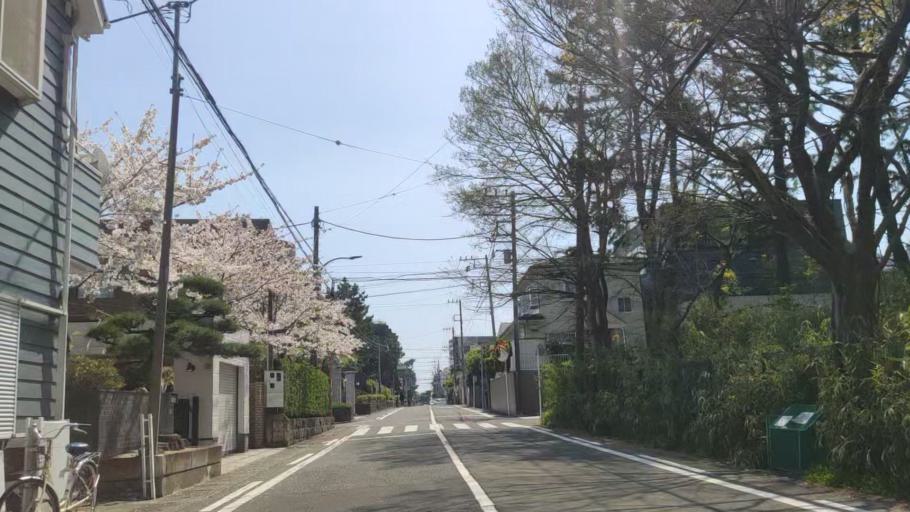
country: JP
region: Kanagawa
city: Hiratsuka
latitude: 35.3218
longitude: 139.3496
